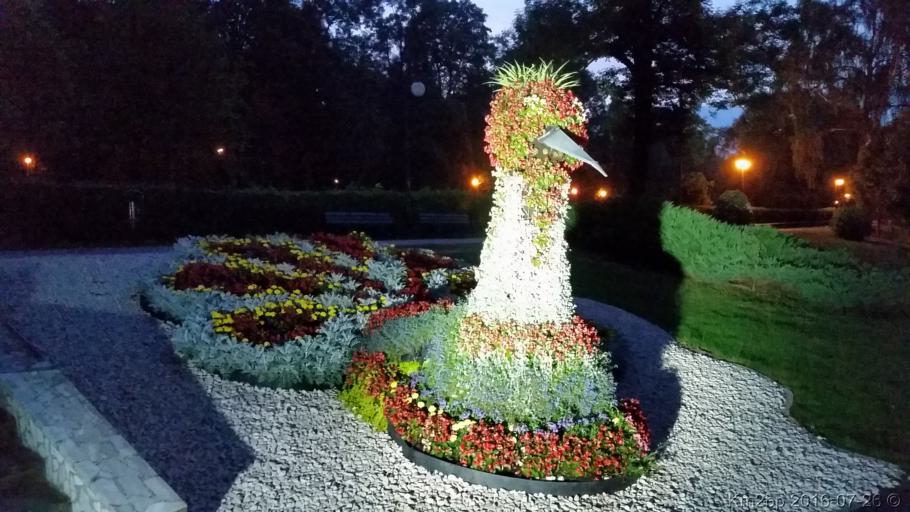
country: PL
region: Subcarpathian Voivodeship
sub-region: Powiat krosnienski
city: Rymanow
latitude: 49.5459
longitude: 21.8502
